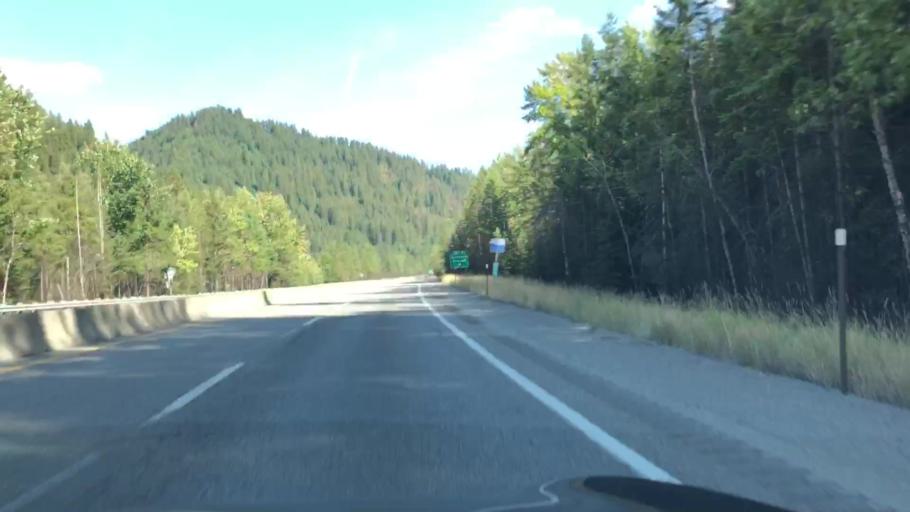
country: US
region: Idaho
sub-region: Shoshone County
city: Wallace
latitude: 47.4746
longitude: -115.8760
